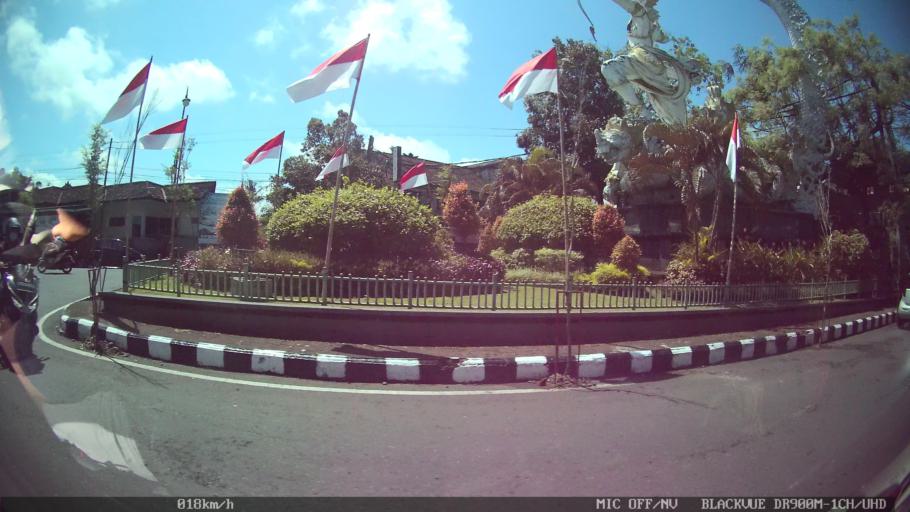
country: ID
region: Bali
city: Banjar Kelodan
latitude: -8.5421
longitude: 115.3329
